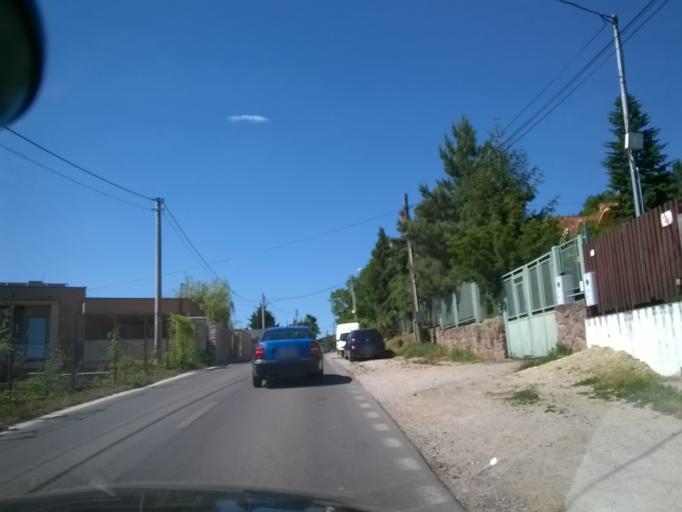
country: SK
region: Nitriansky
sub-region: Okres Nitra
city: Nitra
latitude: 48.3388
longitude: 18.0872
